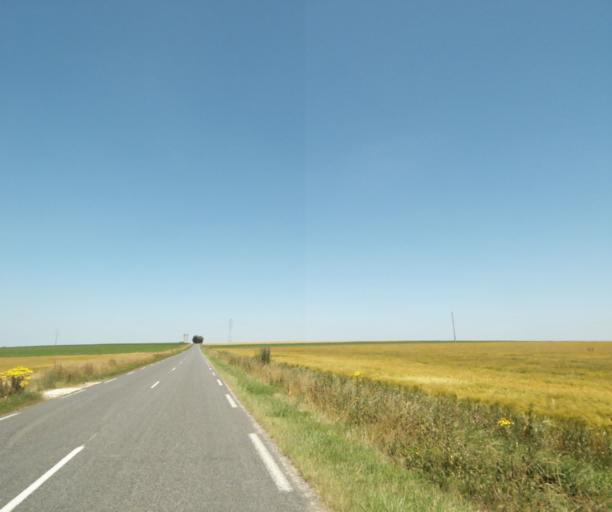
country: FR
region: Centre
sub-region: Departement du Loiret
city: Malesherbes
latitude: 48.3336
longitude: 2.4522
